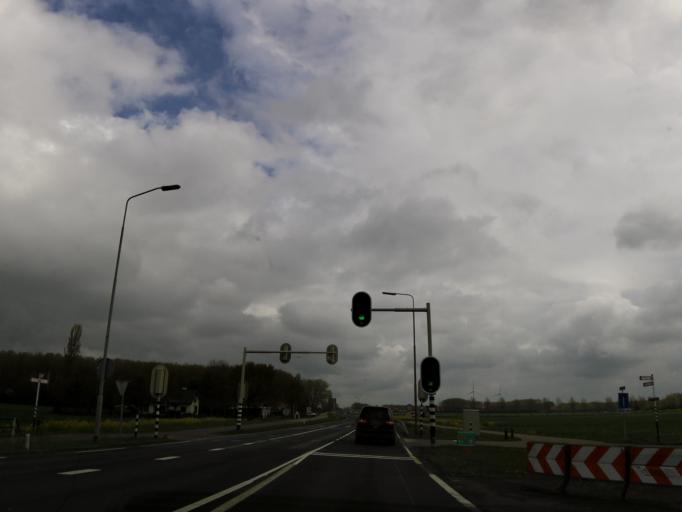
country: NL
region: Gelderland
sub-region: Gemeente Culemborg
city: Culemborg
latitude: 51.9300
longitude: 5.1689
